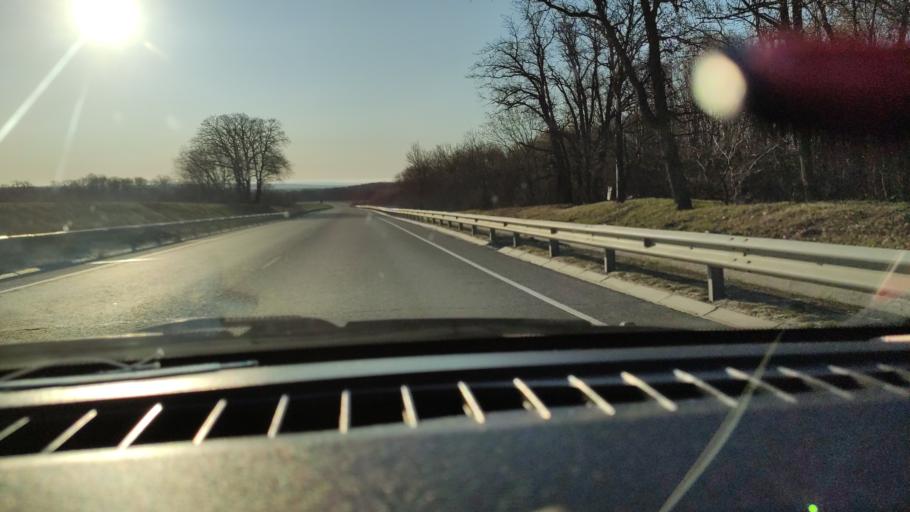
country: RU
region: Saratov
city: Tersa
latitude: 52.1030
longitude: 47.4509
